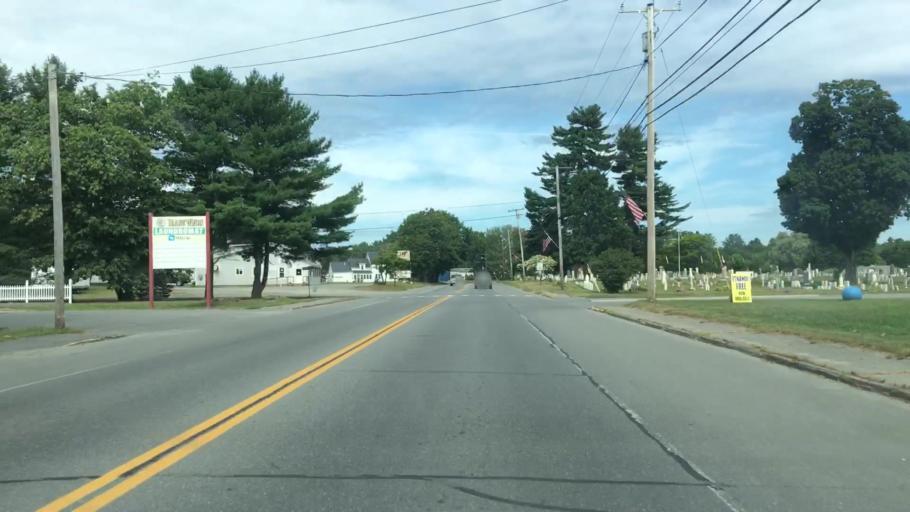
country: US
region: Maine
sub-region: Piscataquis County
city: Milo
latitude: 45.2582
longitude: -68.9874
